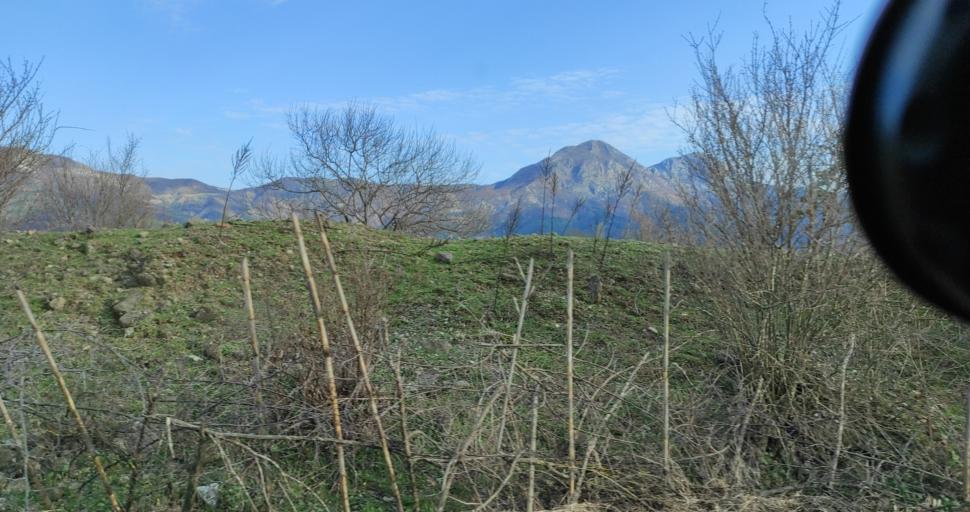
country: AL
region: Lezhe
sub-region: Rrethi i Lezhes
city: Kallmeti i Madh
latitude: 41.8787
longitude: 19.6748
